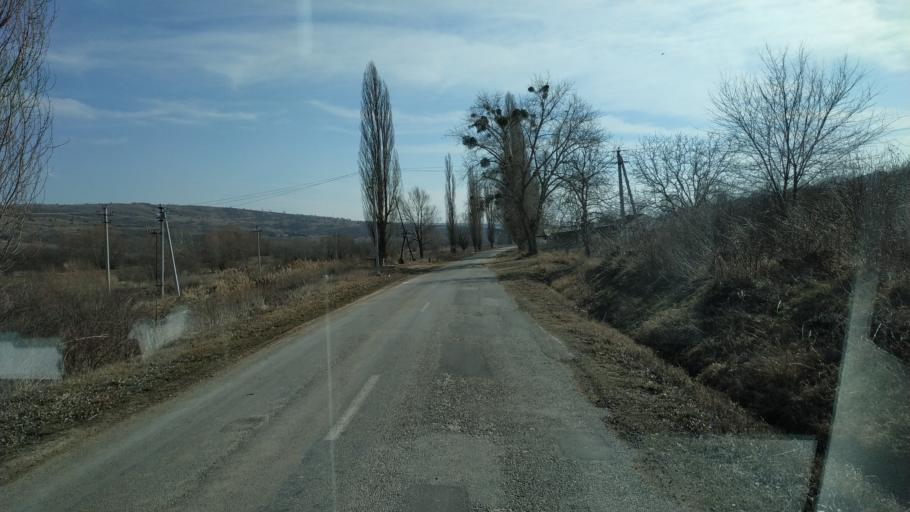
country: MD
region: Nisporeni
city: Nisporeni
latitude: 47.1621
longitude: 28.1027
